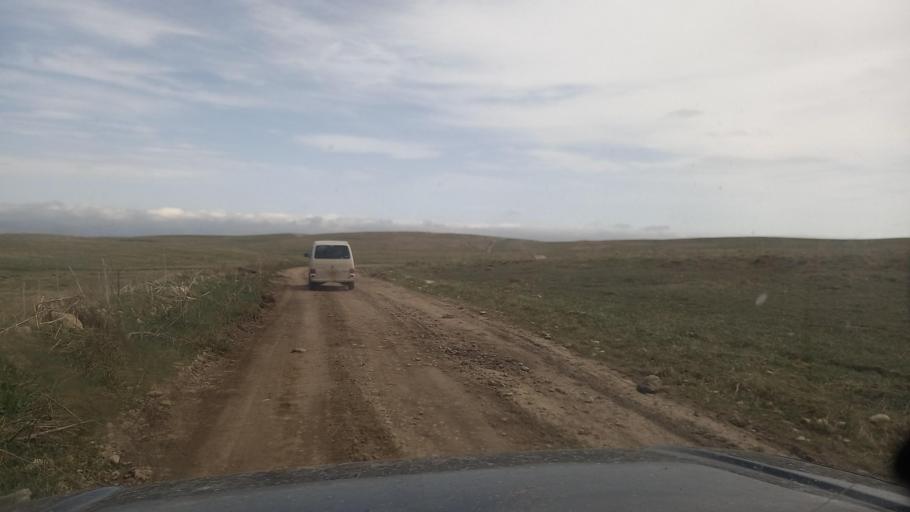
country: RU
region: Stavropol'skiy
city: Kislovodsk
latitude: 43.7529
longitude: 42.7394
